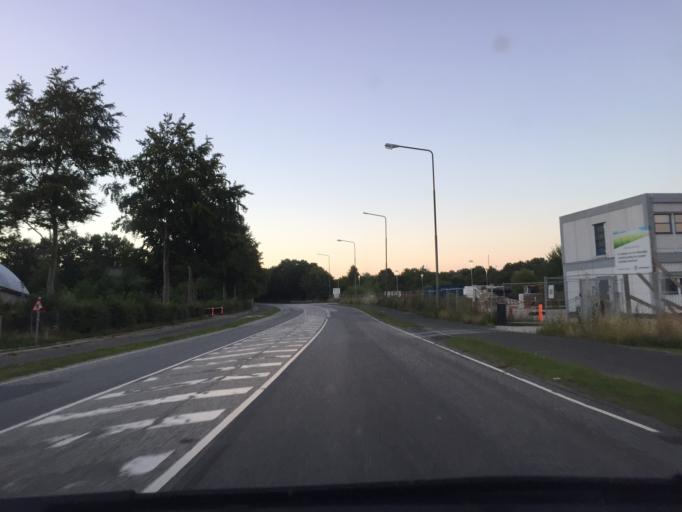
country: DK
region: Capital Region
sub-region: Lyngby-Tarbaek Kommune
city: Kongens Lyngby
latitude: 55.7783
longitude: 12.5235
